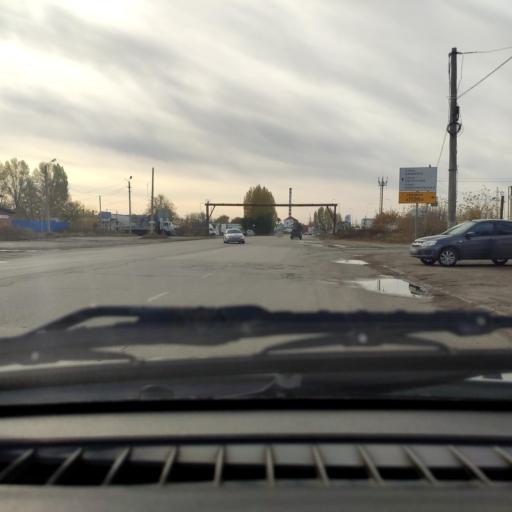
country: RU
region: Samara
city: Tol'yatti
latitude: 53.5247
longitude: 49.4709
